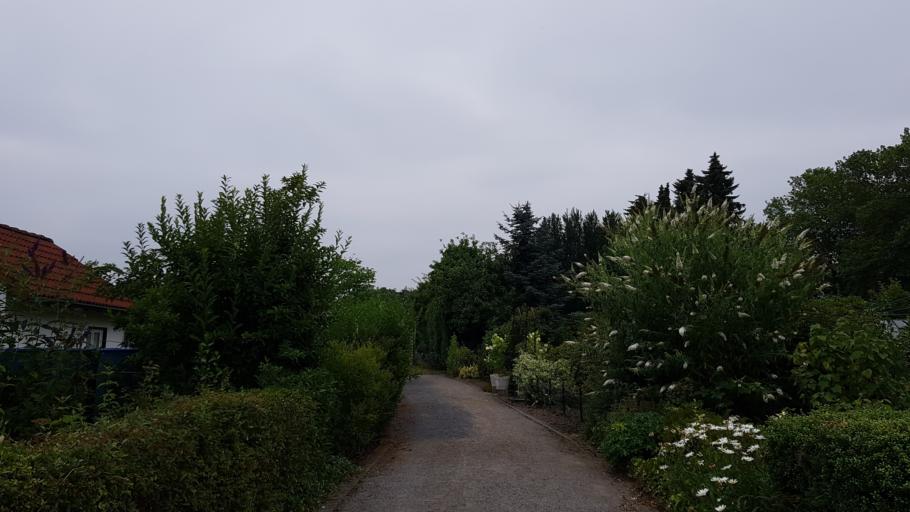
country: DE
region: North Rhine-Westphalia
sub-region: Regierungsbezirk Dusseldorf
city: Muelheim (Ruhr)
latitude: 51.4126
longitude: 6.9093
